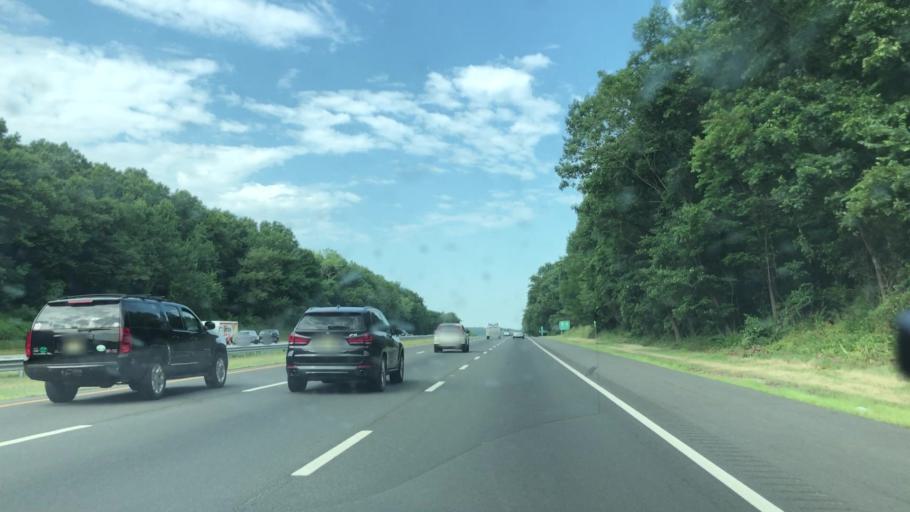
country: US
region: New Jersey
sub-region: Morris County
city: Kenvil
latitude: 40.9016
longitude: -74.6213
